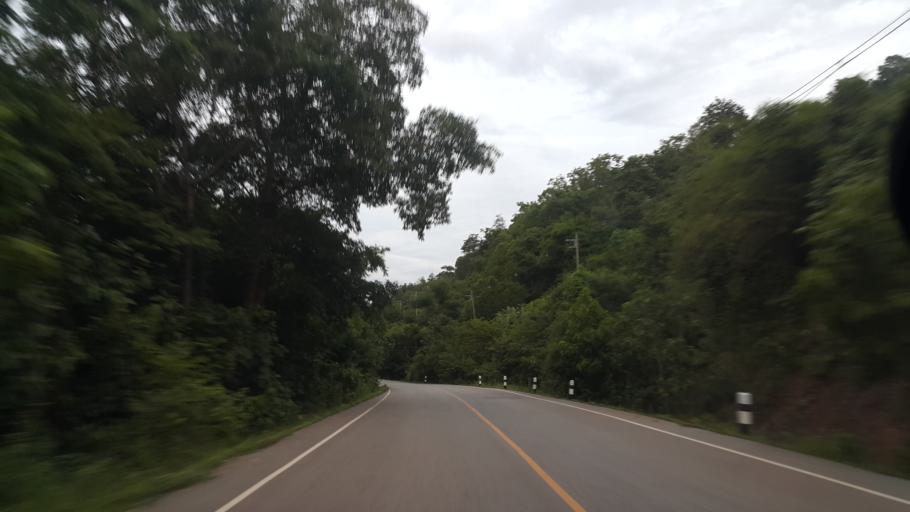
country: TH
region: Loei
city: Na Haeo
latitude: 17.5303
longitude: 101.1923
